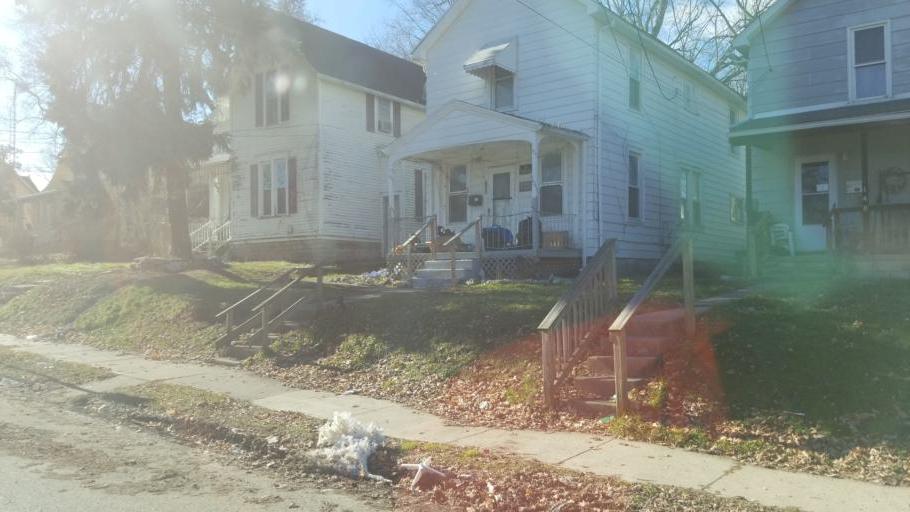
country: US
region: Ohio
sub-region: Richland County
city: Mansfield
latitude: 40.7548
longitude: -82.5248
